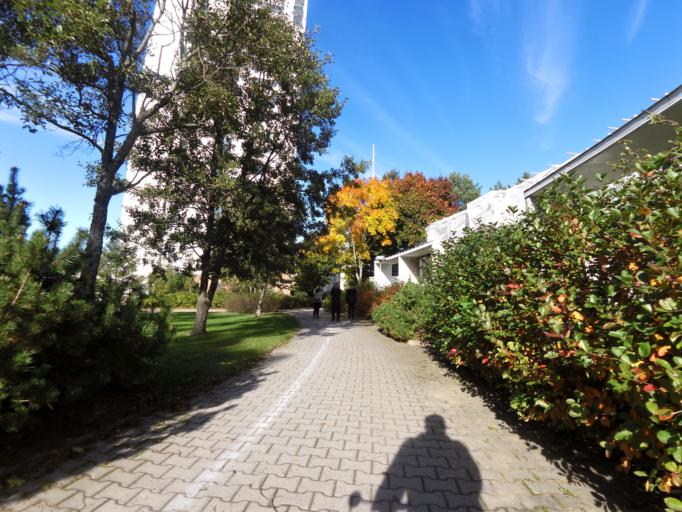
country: FI
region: Uusimaa
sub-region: Helsinki
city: Espoo
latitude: 60.1506
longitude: 24.6349
